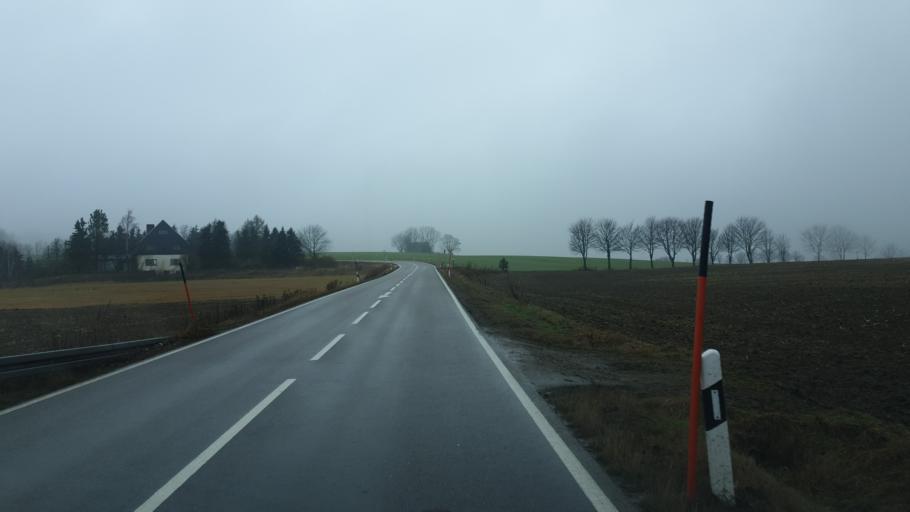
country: DE
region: Saxony
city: Neuhausen
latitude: 50.6667
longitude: 13.4759
